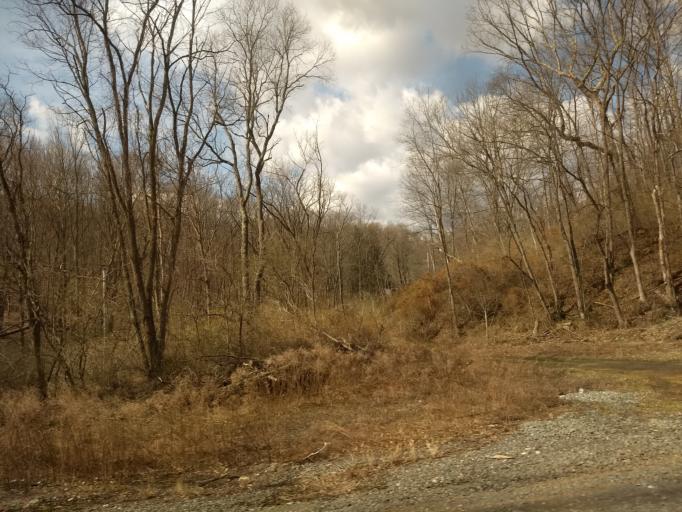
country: US
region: Pennsylvania
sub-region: Blair County
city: Tyrone
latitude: 40.6489
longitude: -78.2006
